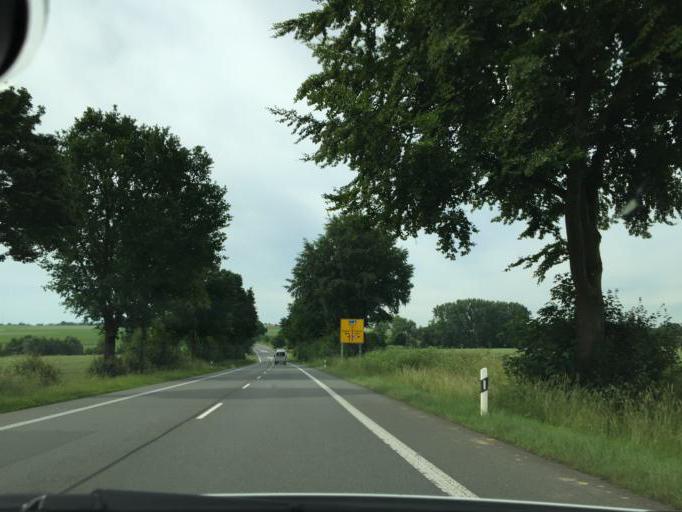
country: DE
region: North Rhine-Westphalia
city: Warburg
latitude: 51.5556
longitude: 9.1328
